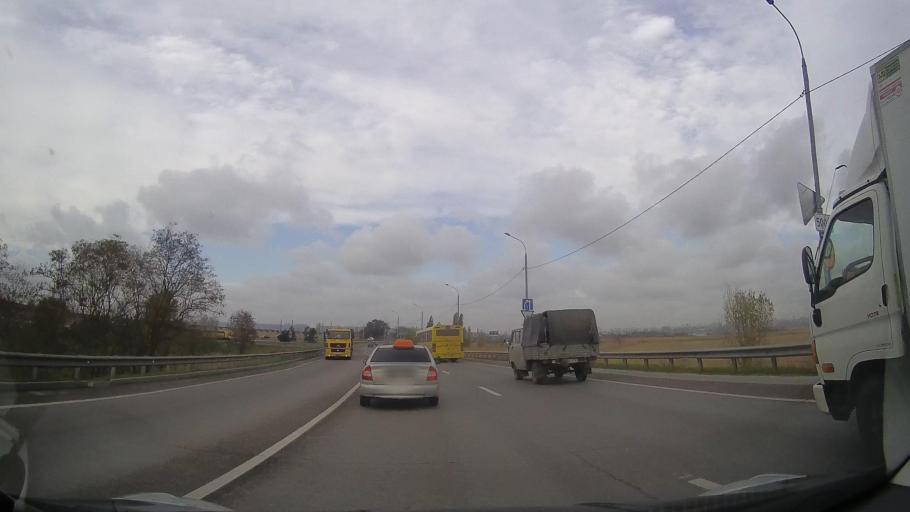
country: RU
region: Rostov
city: Bataysk
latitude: 47.1709
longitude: 39.7469
